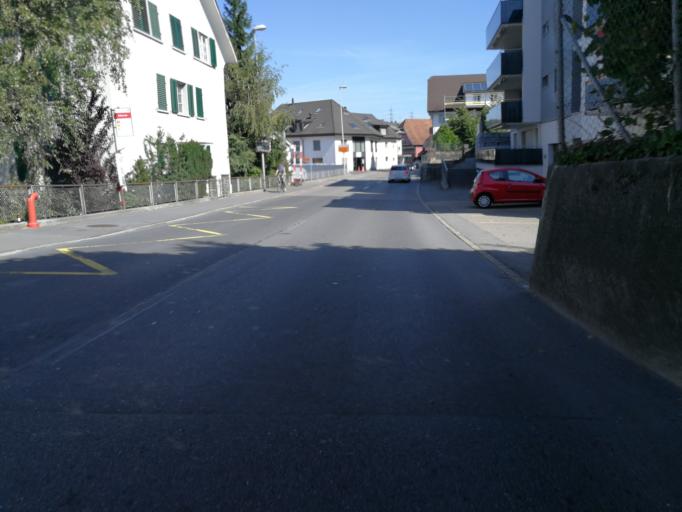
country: CH
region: Schwyz
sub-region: Bezirk Kuessnacht
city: Kussnacht
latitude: 47.0799
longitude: 8.4414
